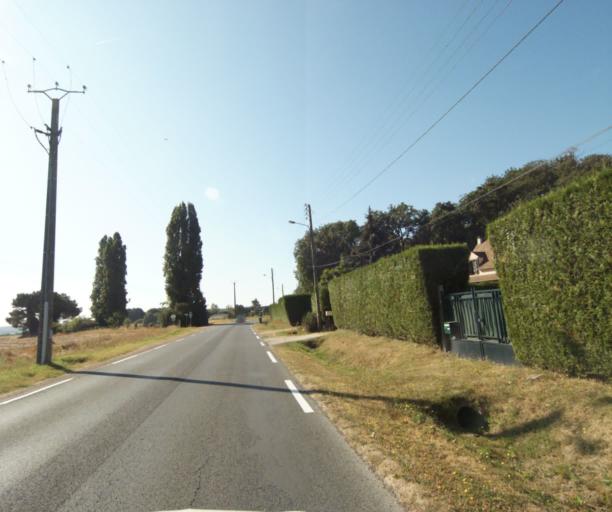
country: FR
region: Ile-de-France
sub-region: Departement de l'Essonne
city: Itteville
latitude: 48.5090
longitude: 2.3455
